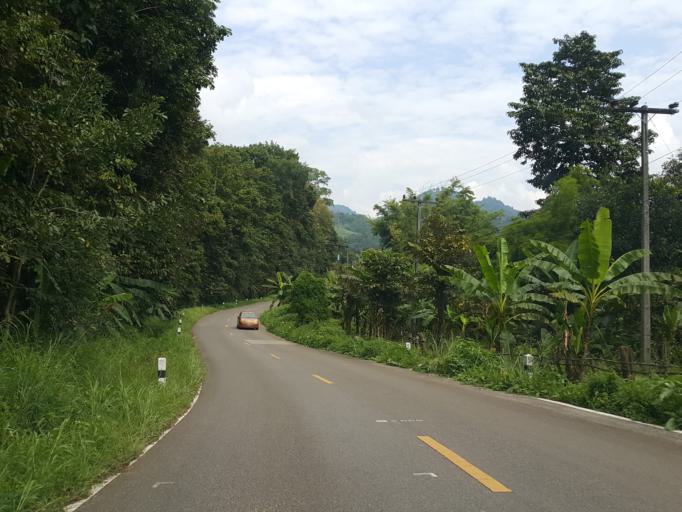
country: TH
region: Mae Hong Son
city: Mae Hong Son
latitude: 19.4720
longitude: 97.9655
